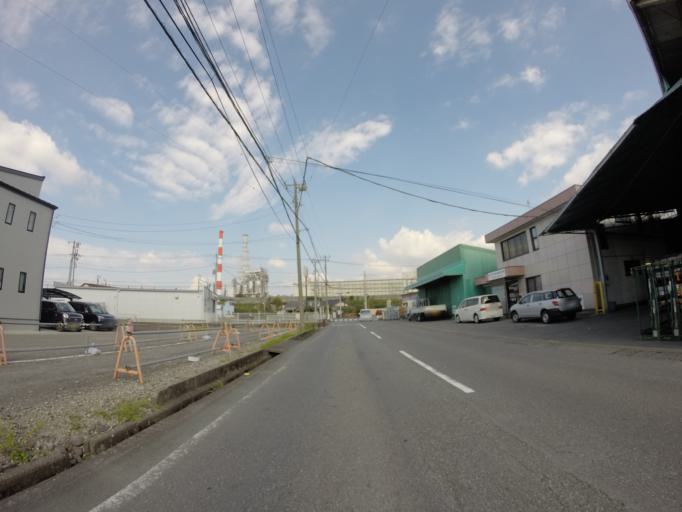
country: JP
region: Shizuoka
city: Fuji
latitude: 35.1424
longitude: 138.6719
